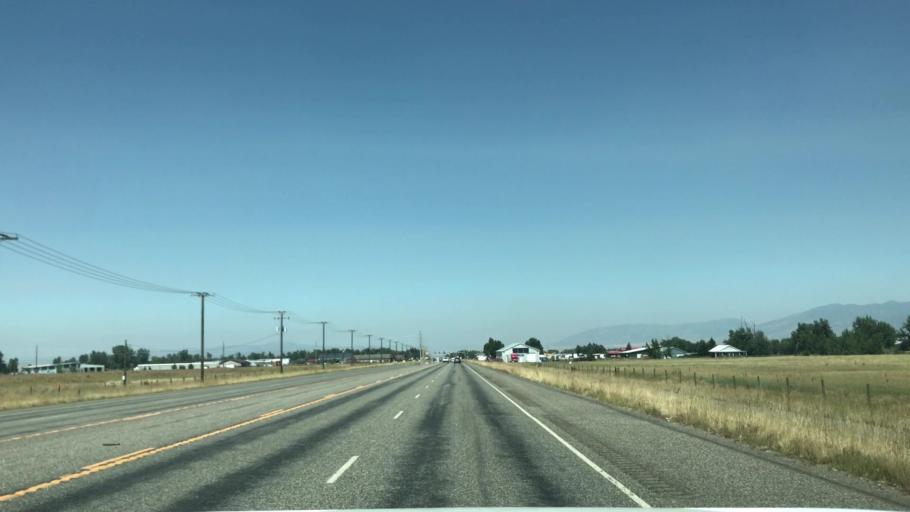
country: US
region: Montana
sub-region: Gallatin County
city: Four Corners
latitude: 45.6936
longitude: -111.1855
